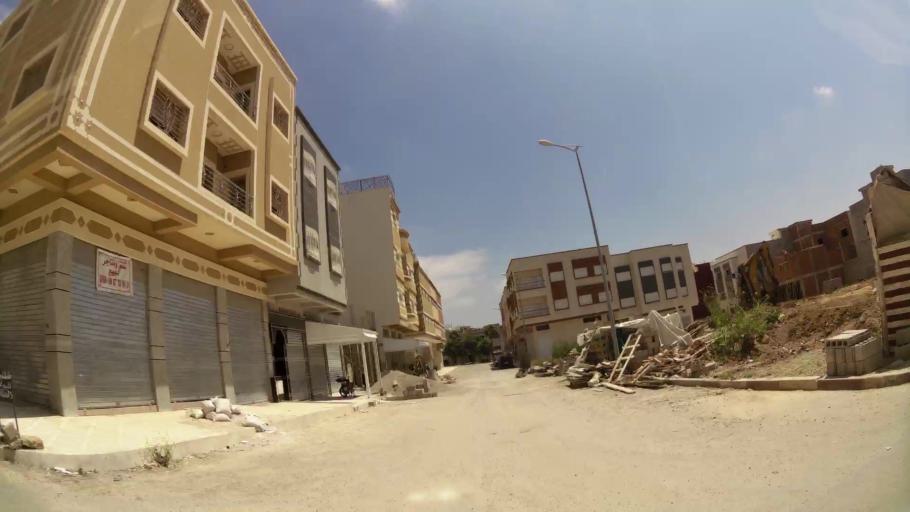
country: MA
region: Fes-Boulemane
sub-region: Fes
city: Fes
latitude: 34.0540
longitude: -5.0376
